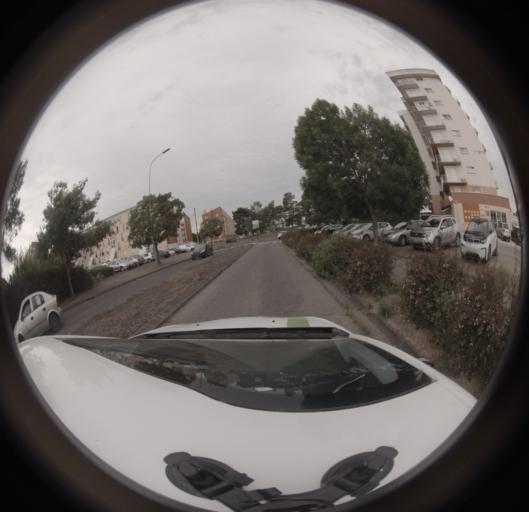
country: FR
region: Midi-Pyrenees
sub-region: Departement du Tarn-et-Garonne
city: Montauban
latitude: 44.0113
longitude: 1.3733
